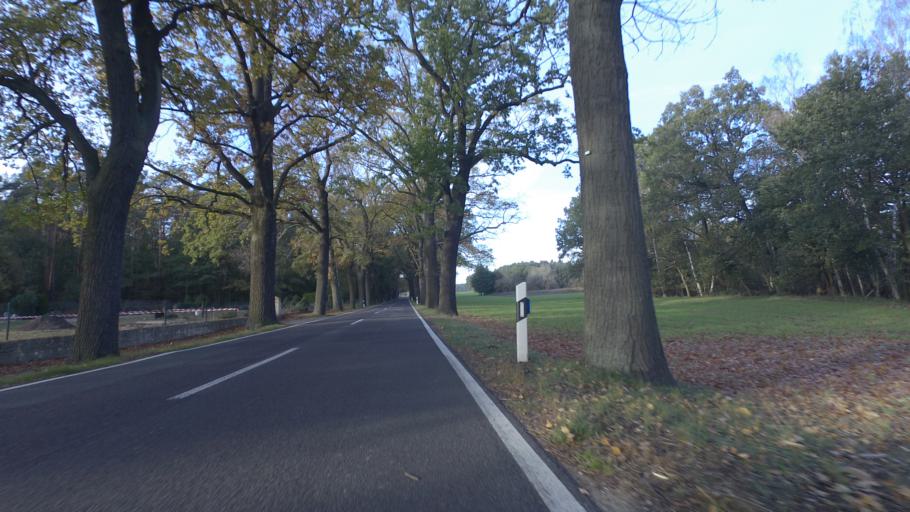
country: DE
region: Brandenburg
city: Sperenberg
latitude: 52.1921
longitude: 13.3191
